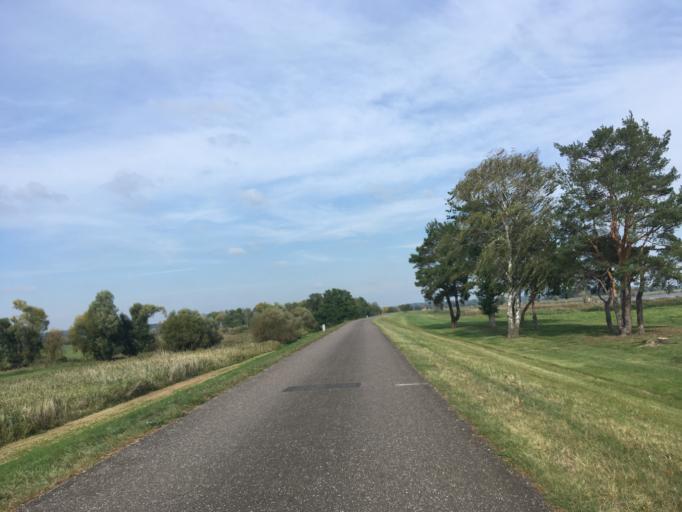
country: DE
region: Brandenburg
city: Schoneberg
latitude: 52.9563
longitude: 14.1377
